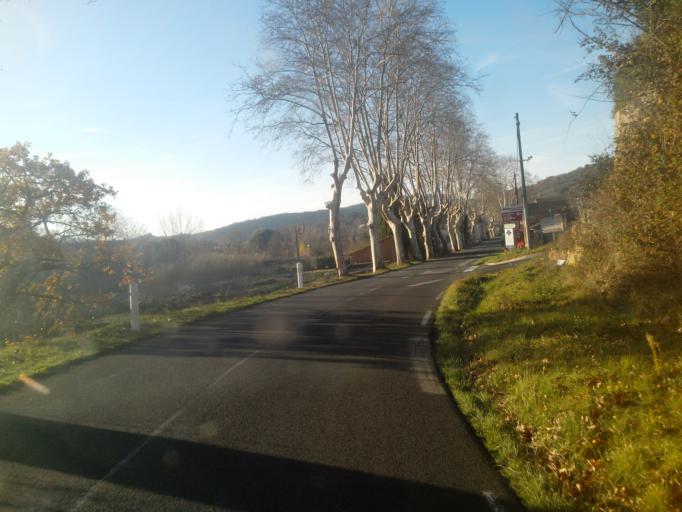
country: FR
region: Languedoc-Roussillon
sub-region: Departement de l'Aude
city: Couiza
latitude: 42.9414
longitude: 2.2604
